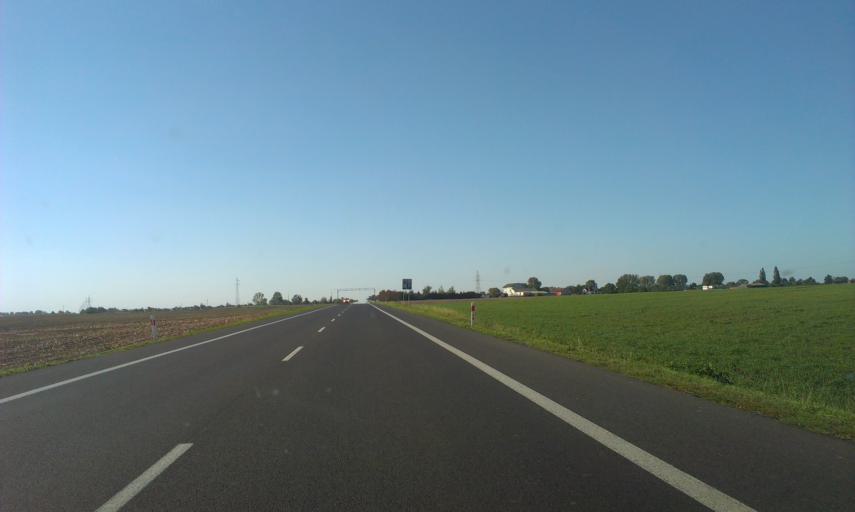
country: PL
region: Kujawsko-Pomorskie
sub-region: Powiat torunski
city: Chelmza
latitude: 53.1635
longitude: 18.5912
